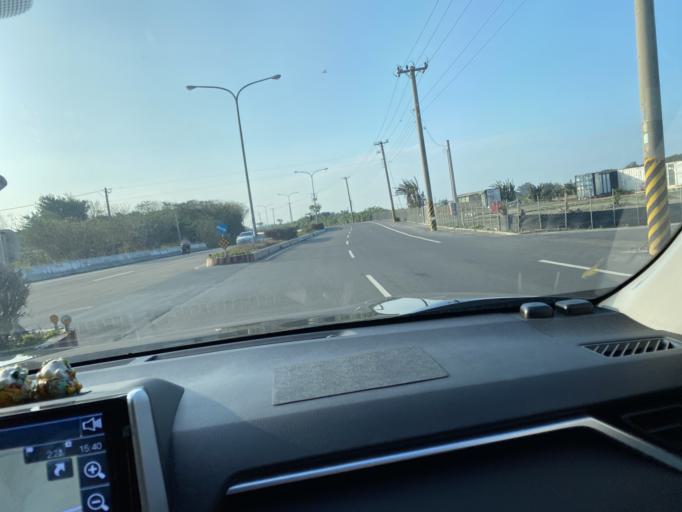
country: TW
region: Taiwan
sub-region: Changhua
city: Chang-hua
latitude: 23.9604
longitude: 120.3606
